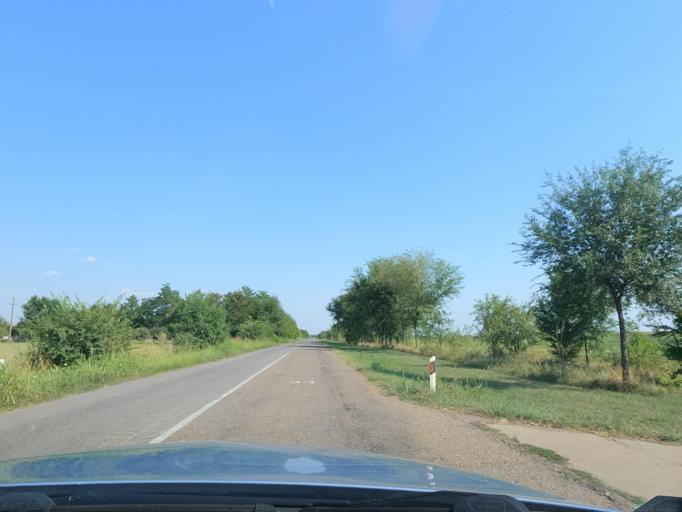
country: RS
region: Autonomna Pokrajina Vojvodina
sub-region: Juznobacki Okrug
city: Becej
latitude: 45.6470
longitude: 19.9832
